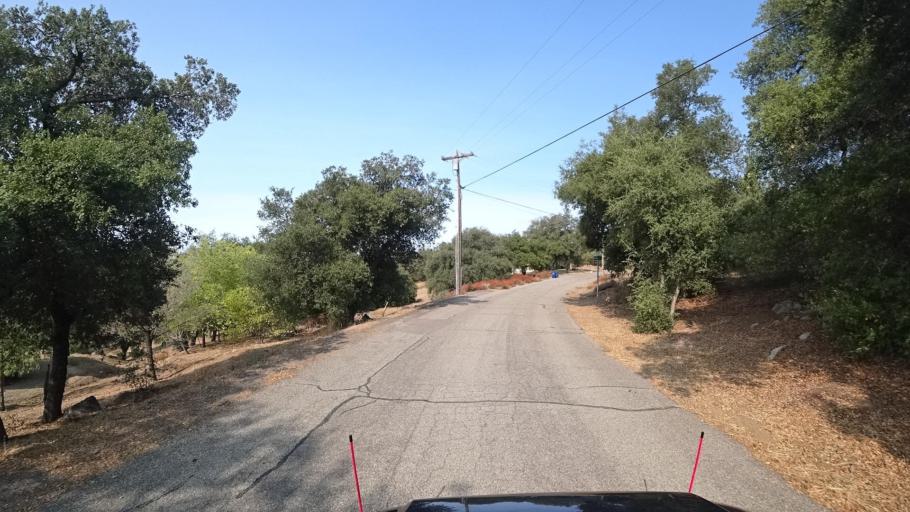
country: US
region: California
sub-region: San Diego County
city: Julian
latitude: 33.0955
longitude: -116.6567
